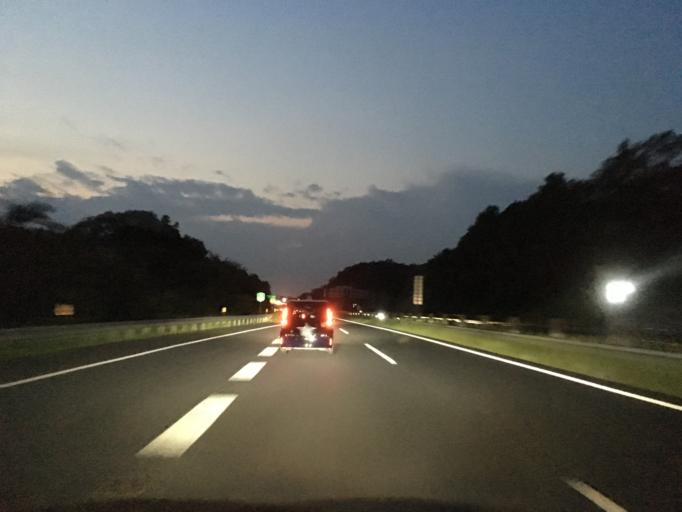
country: JP
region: Chiba
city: Kisarazu
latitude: 35.3818
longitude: 139.9772
